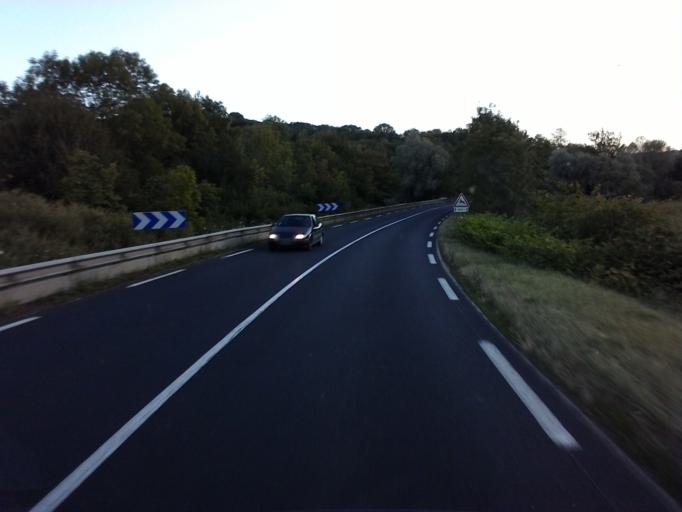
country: FR
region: Franche-Comte
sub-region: Departement du Jura
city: Mouchard
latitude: 47.0083
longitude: 5.8498
